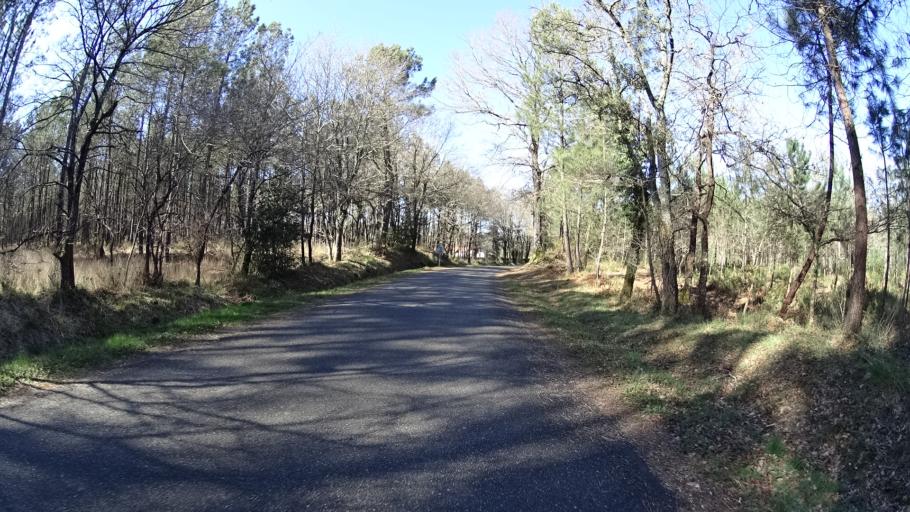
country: FR
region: Aquitaine
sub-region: Departement des Landes
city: Mees
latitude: 43.7407
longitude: -1.0969
